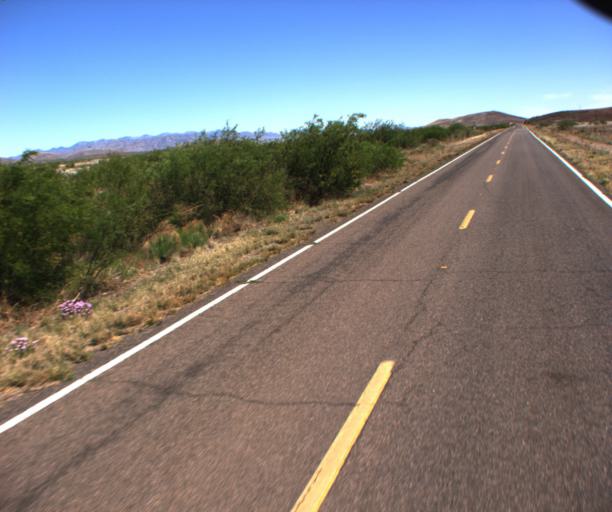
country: US
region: Arizona
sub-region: Cochise County
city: Douglas
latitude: 31.5291
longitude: -109.2969
